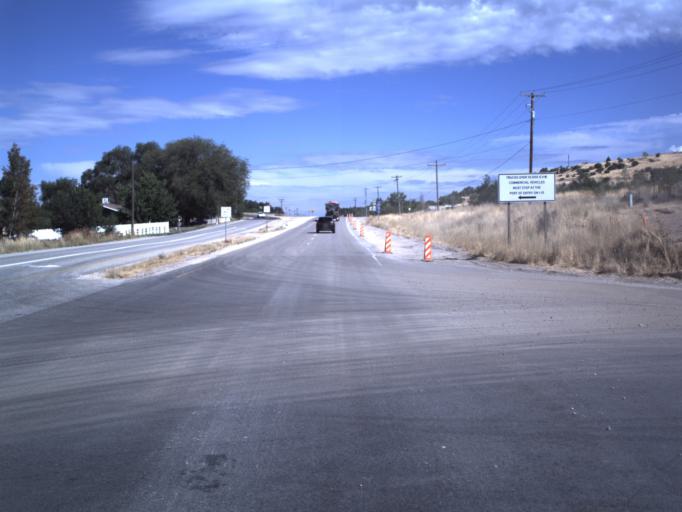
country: US
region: Utah
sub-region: Box Elder County
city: South Willard
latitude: 41.3425
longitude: -112.0317
